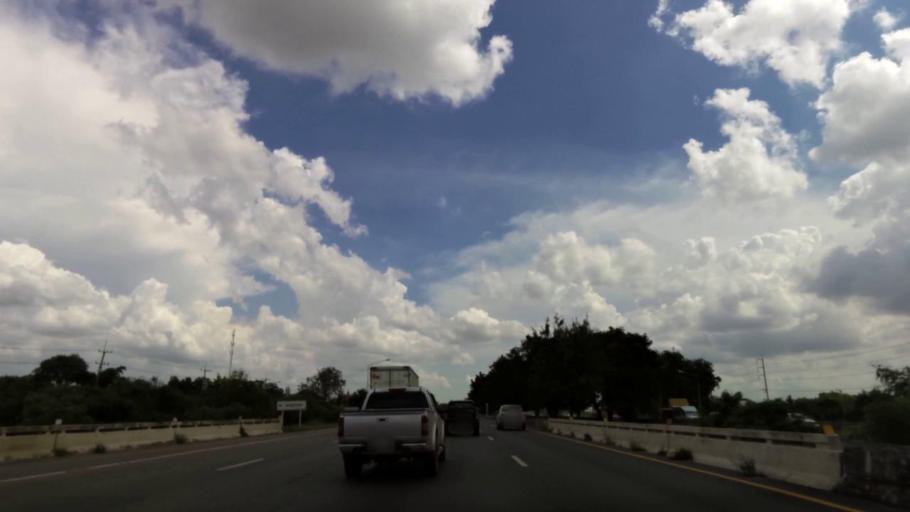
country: TH
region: Phra Nakhon Si Ayutthaya
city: Bang Pahan
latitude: 14.4298
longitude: 100.5534
